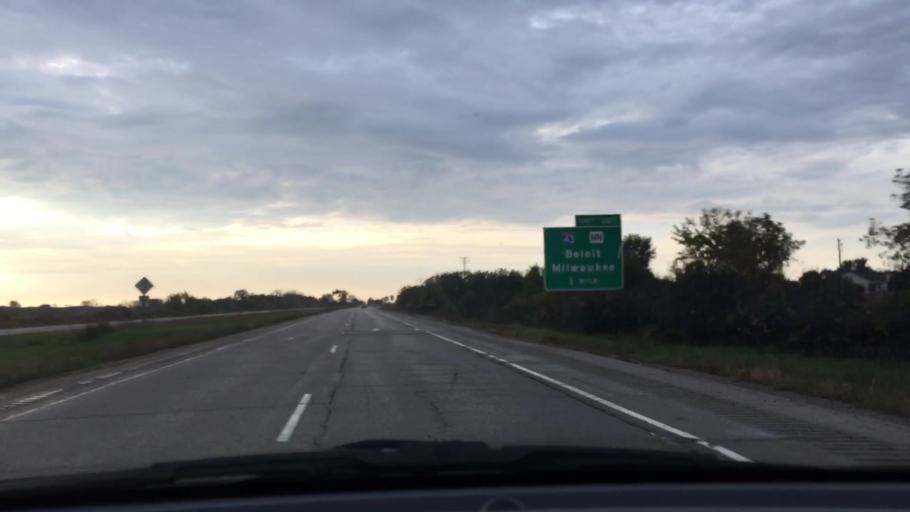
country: US
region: Wisconsin
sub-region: Walworth County
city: Elkhorn
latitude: 42.6932
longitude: -88.5369
